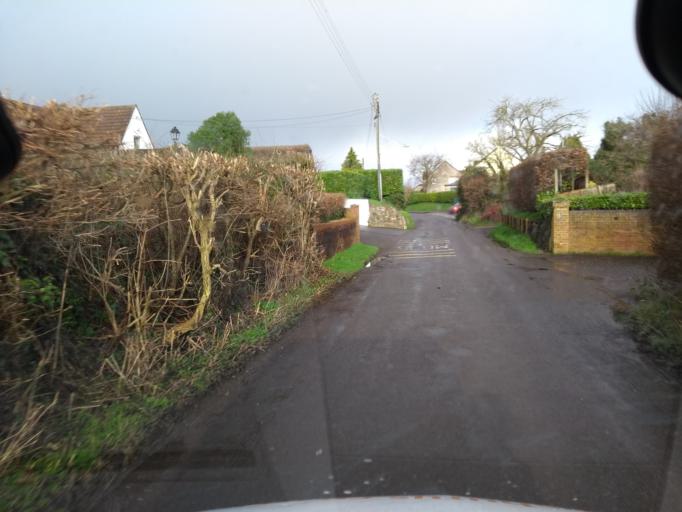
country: GB
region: England
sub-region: Somerset
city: Creech Saint Michael
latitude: 51.0170
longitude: -3.0498
